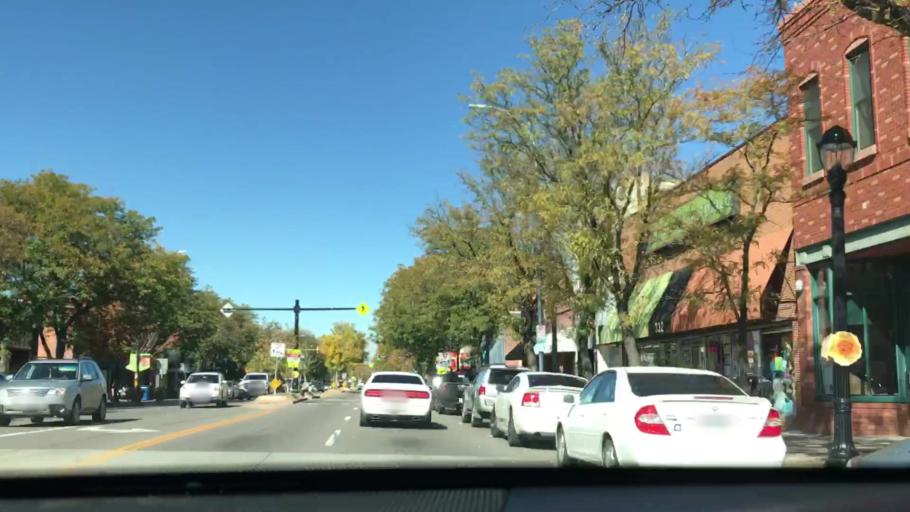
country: US
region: Colorado
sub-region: Boulder County
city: Longmont
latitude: 40.1644
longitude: -105.1025
